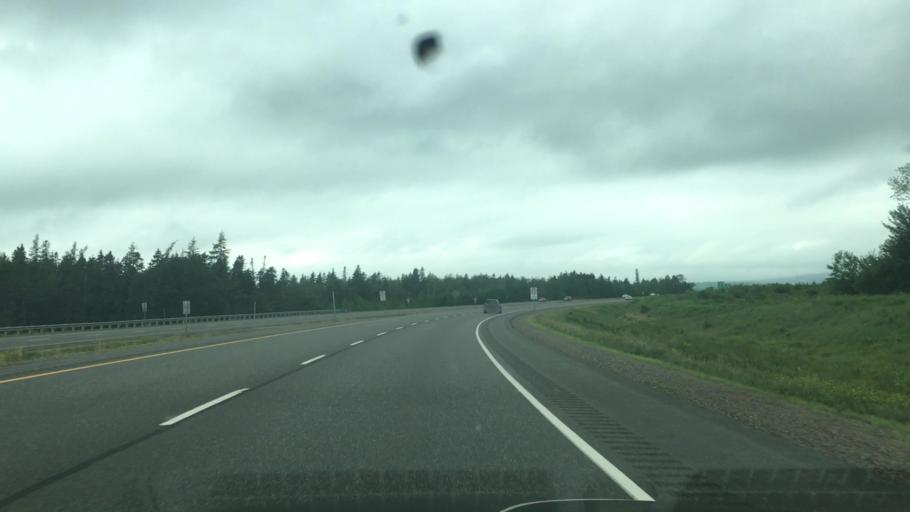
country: CA
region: Nova Scotia
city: Truro
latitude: 45.4322
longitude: -63.5765
